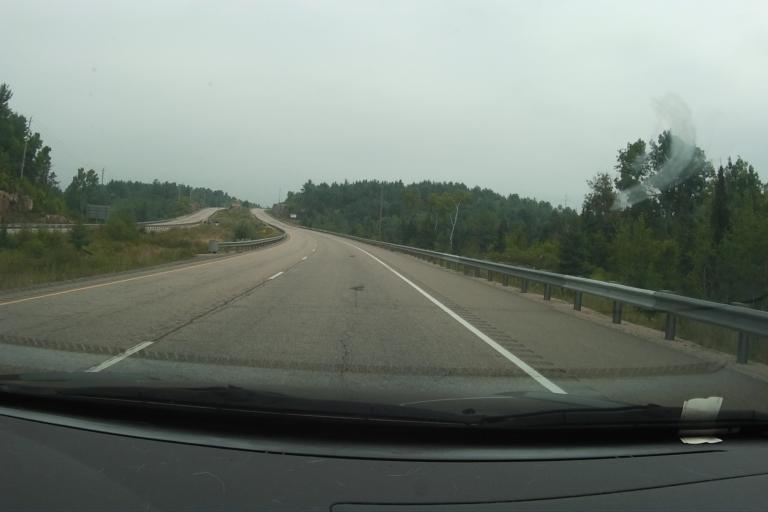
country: CA
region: Ontario
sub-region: Nipissing District
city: North Bay
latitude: 46.2081
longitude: -79.3484
